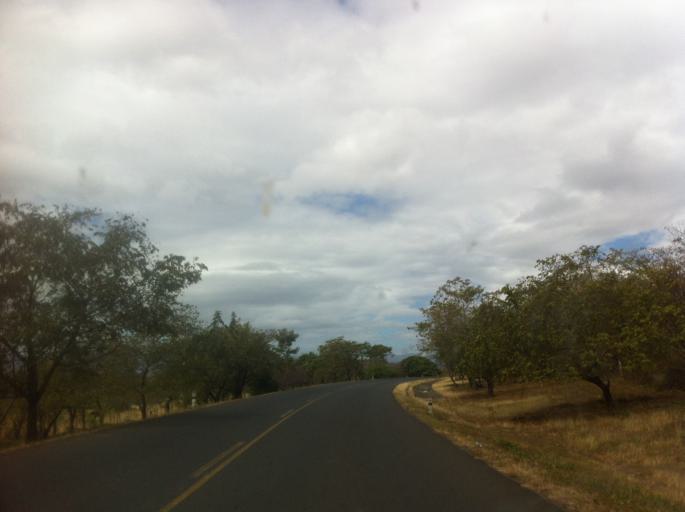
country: NI
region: Chontales
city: Juigalpa
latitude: 12.0832
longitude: -85.3329
